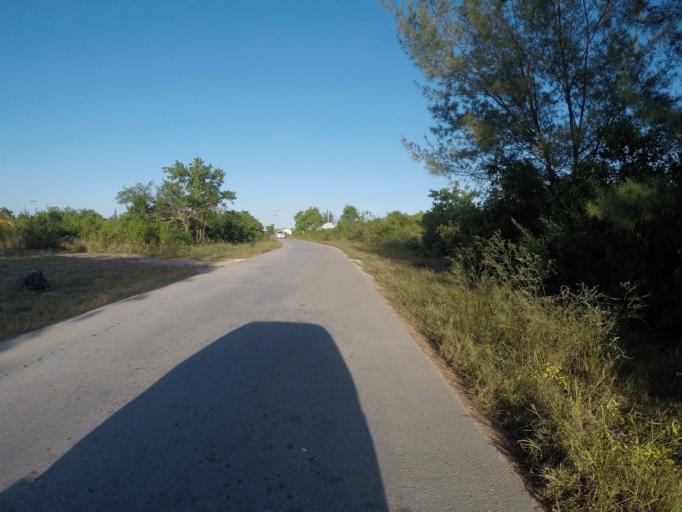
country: TZ
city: Kiwengwa
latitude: -6.1447
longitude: 39.4985
